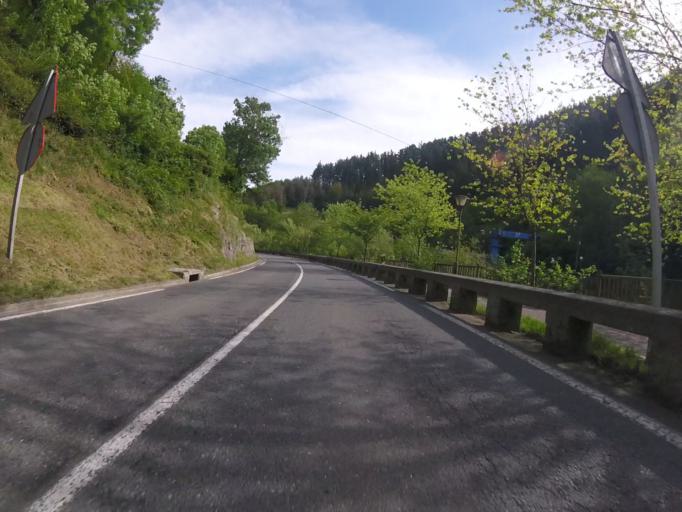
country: ES
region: Basque Country
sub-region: Provincia de Guipuzcoa
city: Urretxu
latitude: 43.1030
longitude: -2.3170
